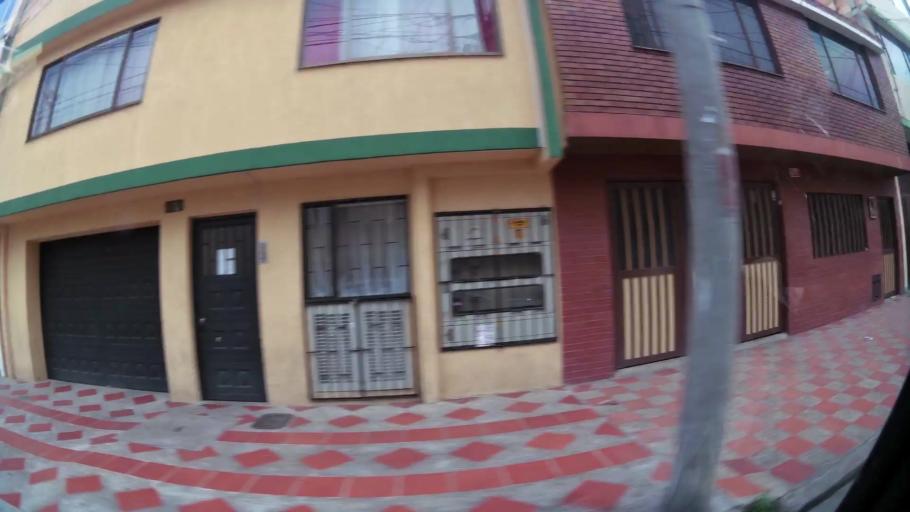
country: CO
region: Bogota D.C.
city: Barrio San Luis
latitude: 4.7238
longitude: -74.0704
